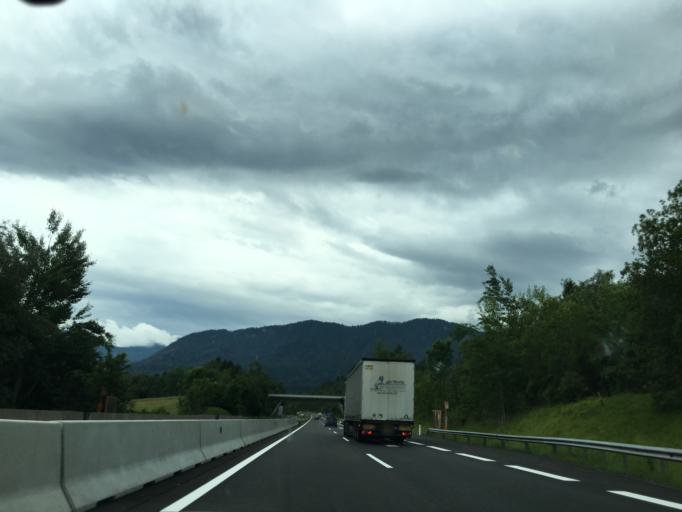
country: AT
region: Carinthia
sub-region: Politischer Bezirk Villach Land
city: Rosegg
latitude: 46.5634
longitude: 14.0063
